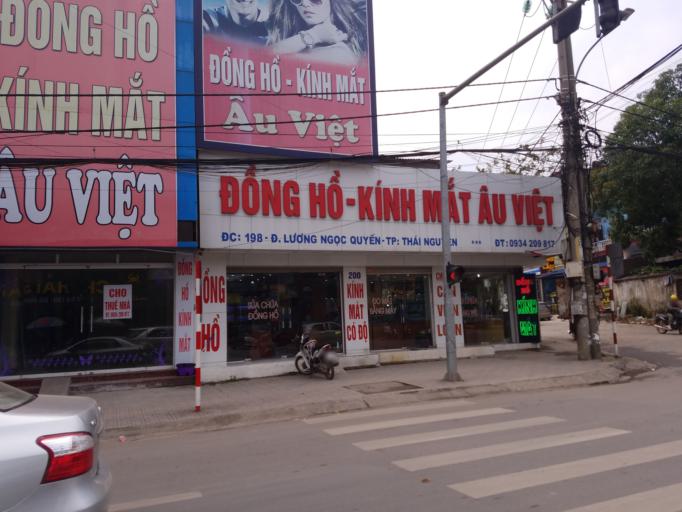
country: VN
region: Thai Nguyen
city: Thanh Pho Thai Nguyen
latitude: 21.5934
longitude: 105.8251
